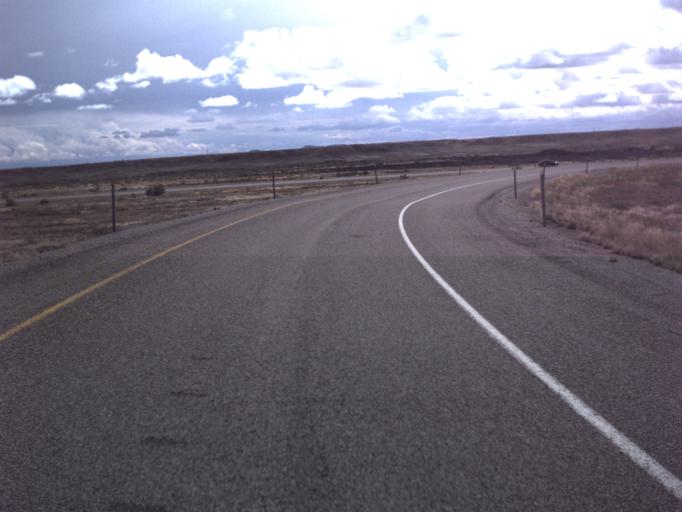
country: US
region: Utah
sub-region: Carbon County
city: East Carbon City
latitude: 38.9831
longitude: -110.2368
